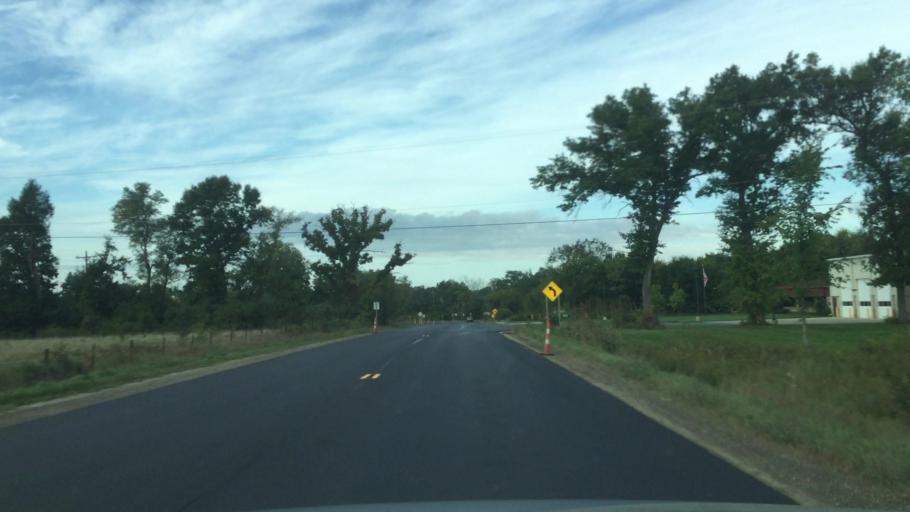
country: US
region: Michigan
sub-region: Oakland County
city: Holly
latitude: 42.8141
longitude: -83.6057
